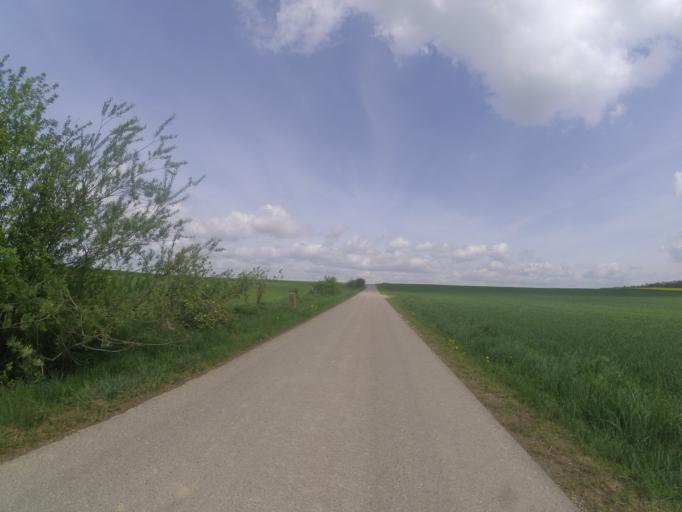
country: DE
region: Baden-Wuerttemberg
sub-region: Tuebingen Region
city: Griesingen
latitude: 48.2511
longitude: 9.7770
